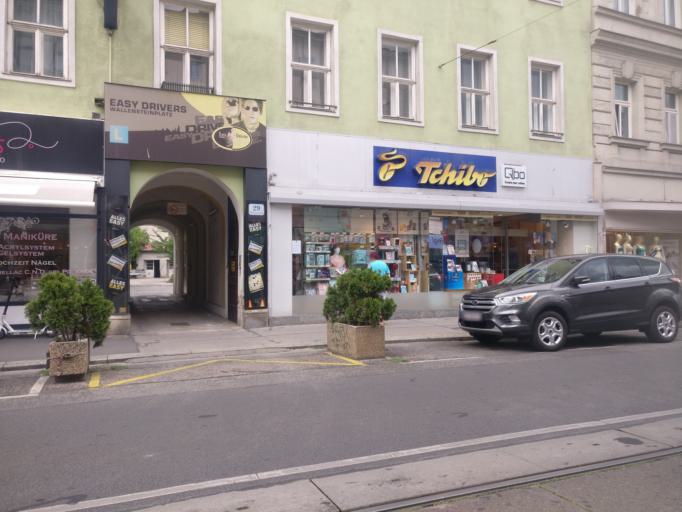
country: AT
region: Vienna
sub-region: Wien Stadt
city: Vienna
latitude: 48.2298
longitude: 16.3705
